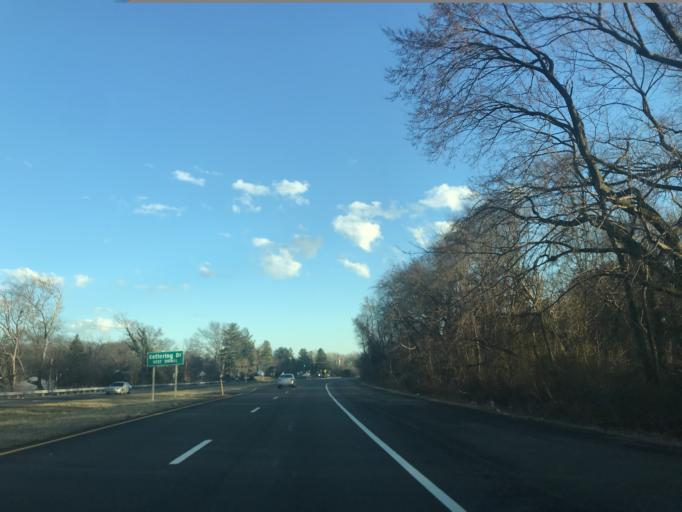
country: US
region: Maryland
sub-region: Prince George's County
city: Kettering
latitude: 38.8860
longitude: -76.8165
